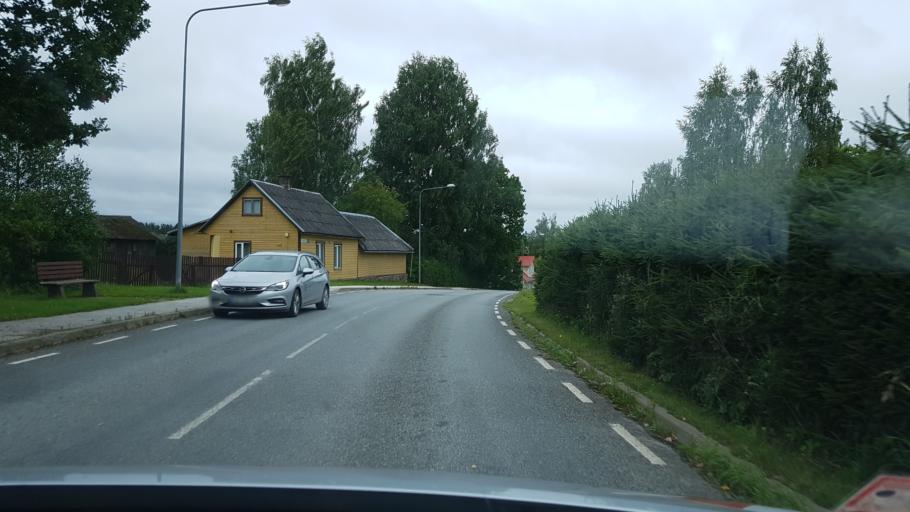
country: EE
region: Vorumaa
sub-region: Antsla vald
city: Vana-Antsla
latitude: 57.9878
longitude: 26.7520
